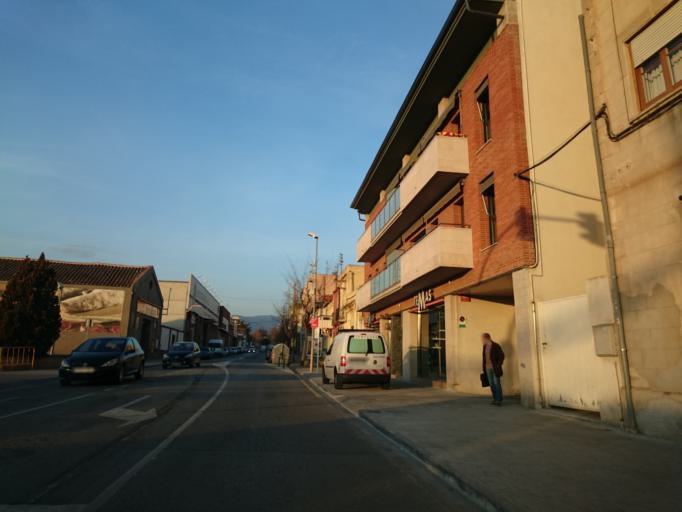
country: ES
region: Catalonia
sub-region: Provincia de Barcelona
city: Les Franqueses del Valles
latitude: 41.6302
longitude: 2.2955
